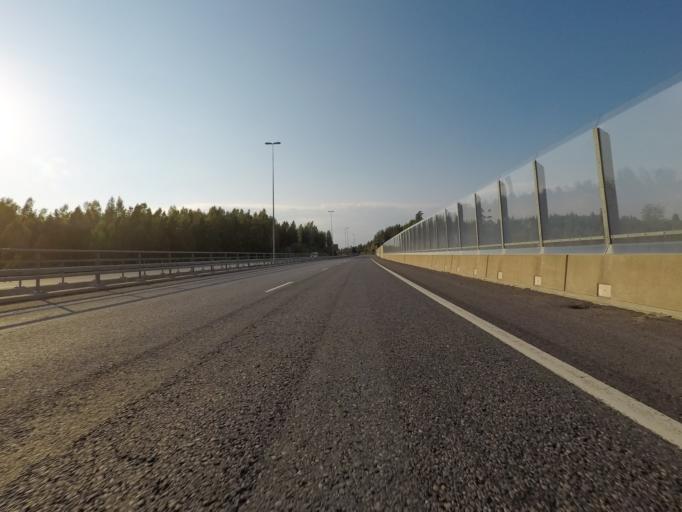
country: FI
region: Uusimaa
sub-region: Helsinki
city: Saukkola
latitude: 60.3180
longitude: 23.9687
